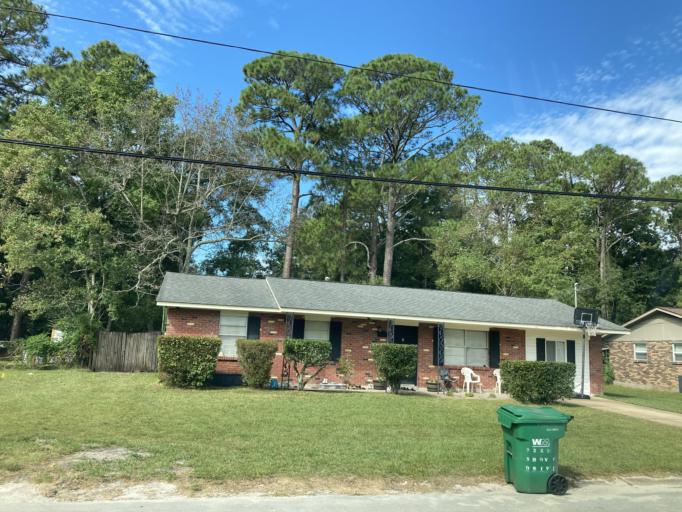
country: US
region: Mississippi
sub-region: Jackson County
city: Saint Martin
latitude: 30.4469
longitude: -88.8757
